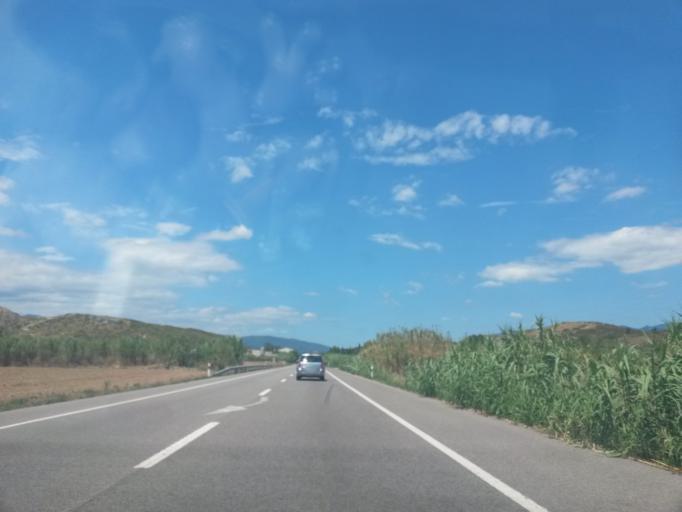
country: ES
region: Catalonia
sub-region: Provincia de Girona
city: Biure
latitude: 42.3410
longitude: 2.9172
